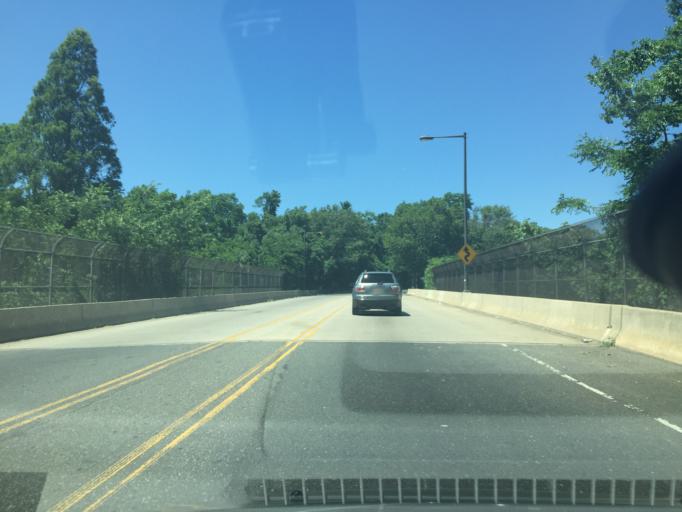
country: US
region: Pennsylvania
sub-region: Philadelphia County
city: Philadelphia
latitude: 39.9767
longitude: -75.1894
